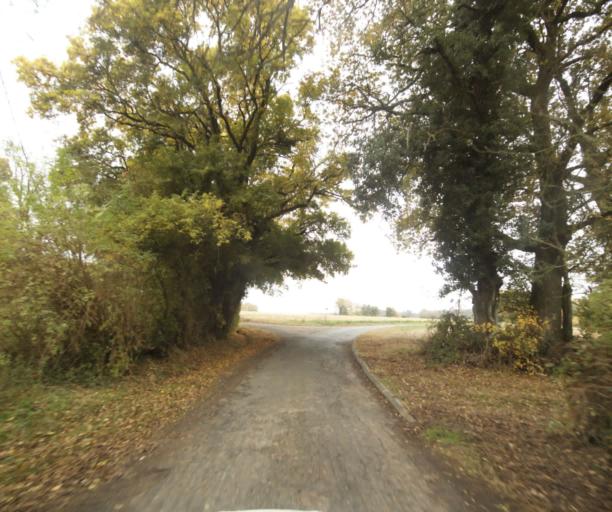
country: FR
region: Poitou-Charentes
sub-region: Departement de la Charente-Maritime
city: Saint-Georges-des-Coteaux
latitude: 45.7393
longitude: -0.6894
